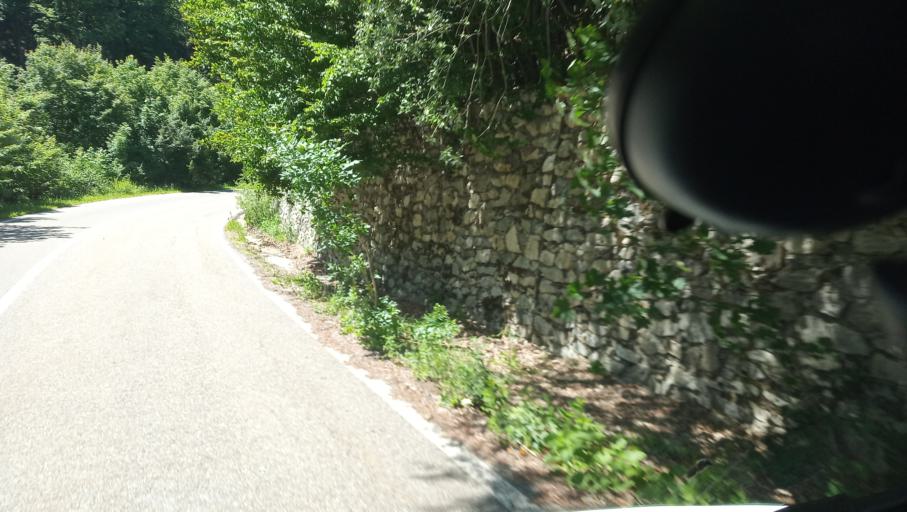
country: RO
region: Mehedinti
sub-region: Comuna Isverna
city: Isverna
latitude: 45.0538
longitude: 22.6117
